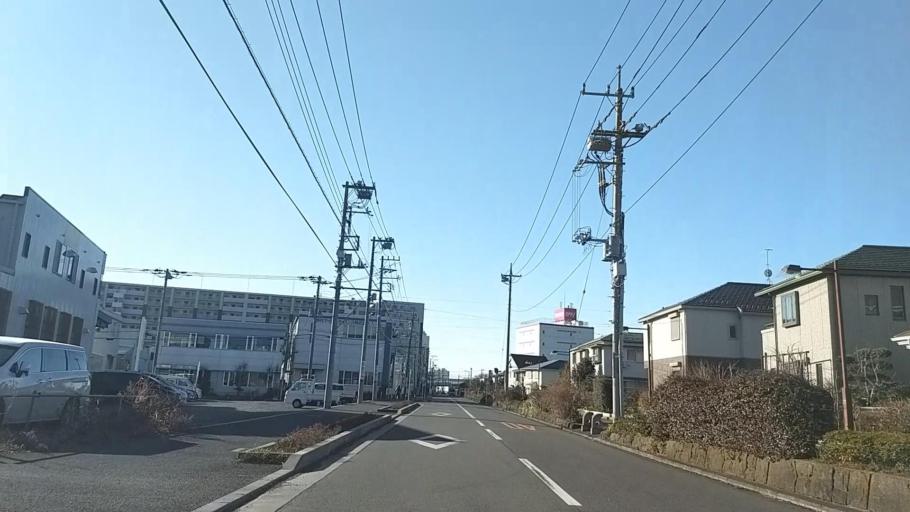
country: JP
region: Kanagawa
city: Atsugi
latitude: 35.4296
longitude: 139.3592
